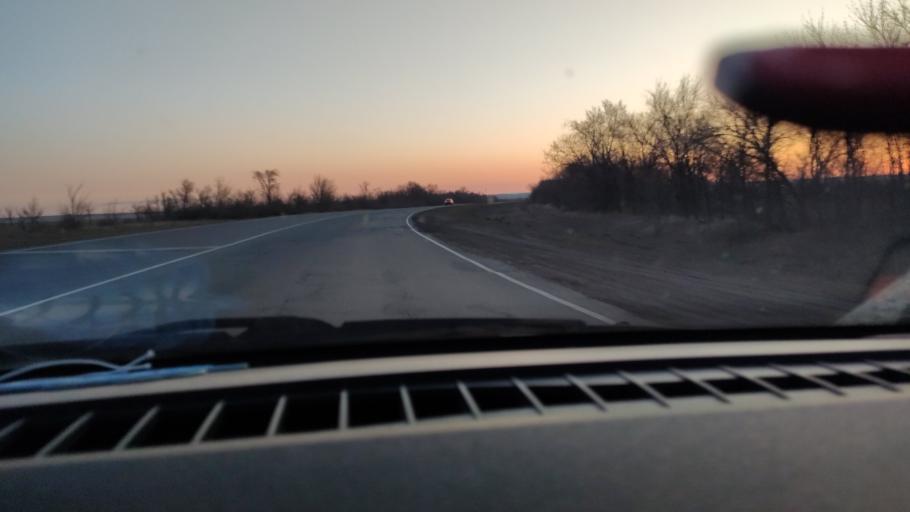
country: RU
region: Saratov
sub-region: Saratovskiy Rayon
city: Saratov
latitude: 51.7076
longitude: 46.0151
